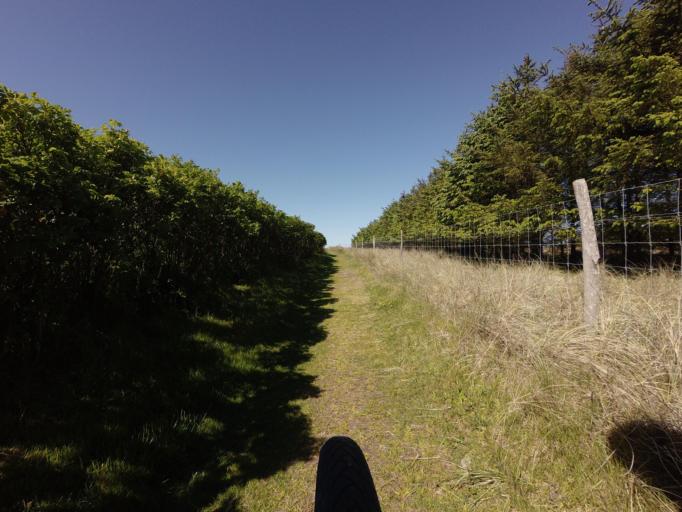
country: DK
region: North Denmark
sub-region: Jammerbugt Kommune
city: Pandrup
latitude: 57.3127
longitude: 9.6624
